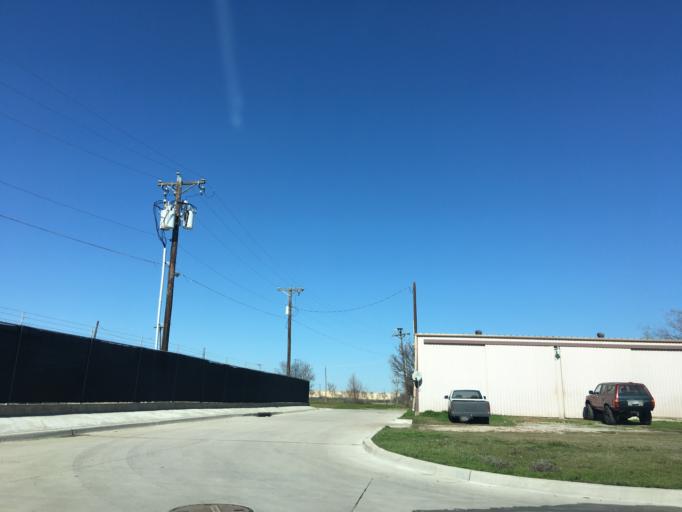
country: US
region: Texas
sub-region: Collin County
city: Prosper
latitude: 33.2355
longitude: -96.8042
